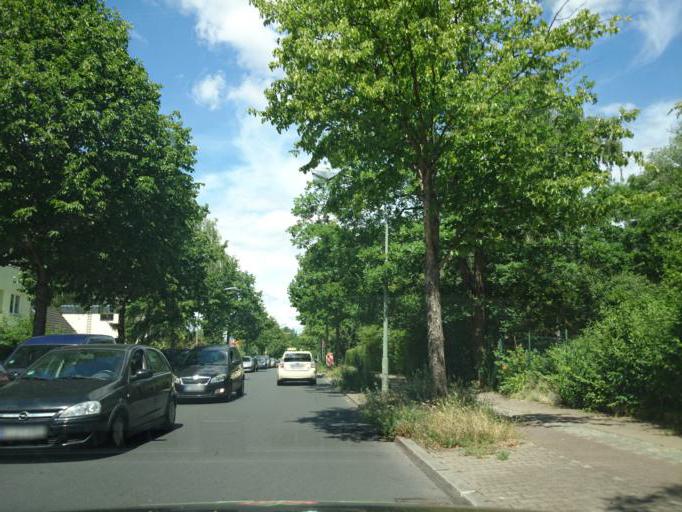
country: DE
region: Berlin
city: Lichtenrade
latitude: 52.3970
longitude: 13.3898
